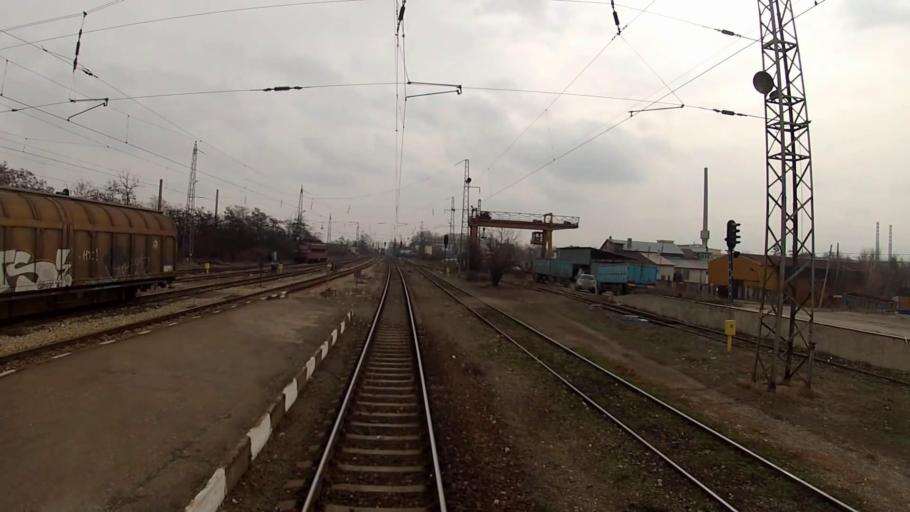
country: BG
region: Sofia-Capital
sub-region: Stolichna Obshtina
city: Sofia
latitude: 42.6561
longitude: 23.4518
